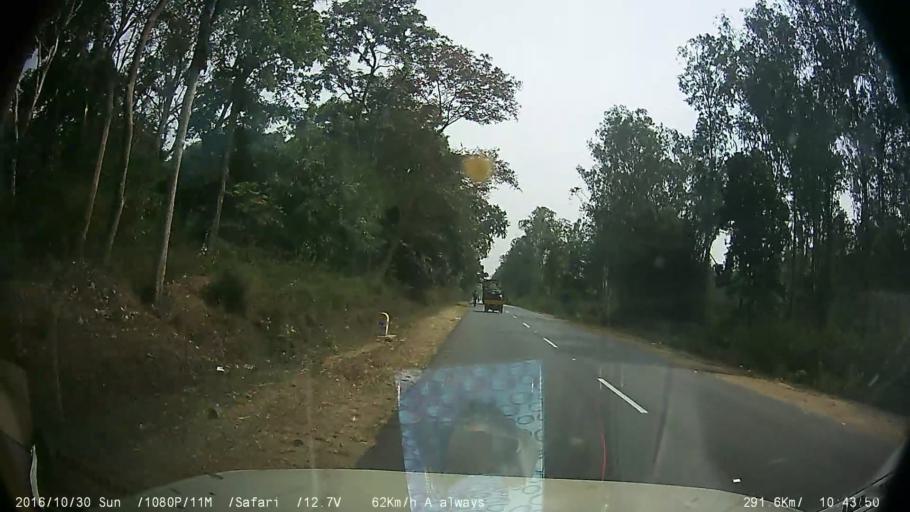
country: IN
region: Karnataka
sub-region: Kodagu
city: Kushalnagar
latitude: 12.4370
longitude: 75.9011
